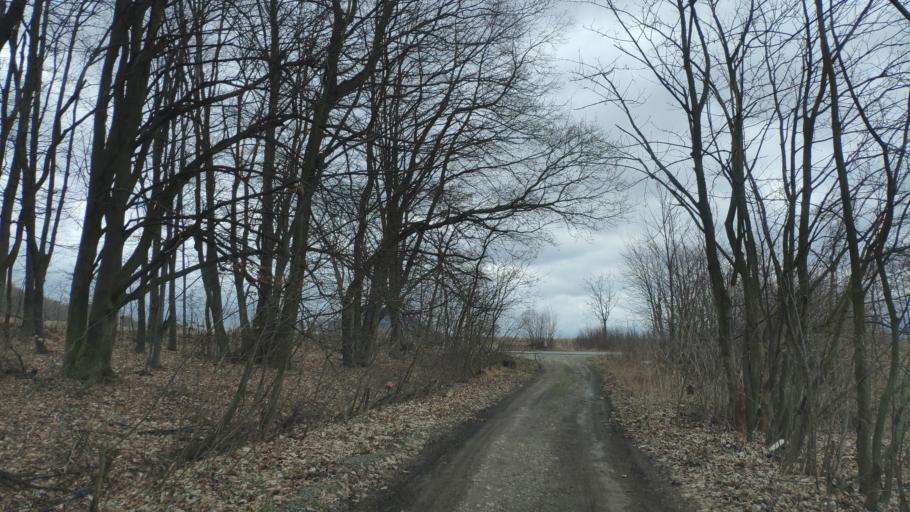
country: SK
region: Presovsky
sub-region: Okres Presov
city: Presov
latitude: 49.0763
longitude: 21.2691
